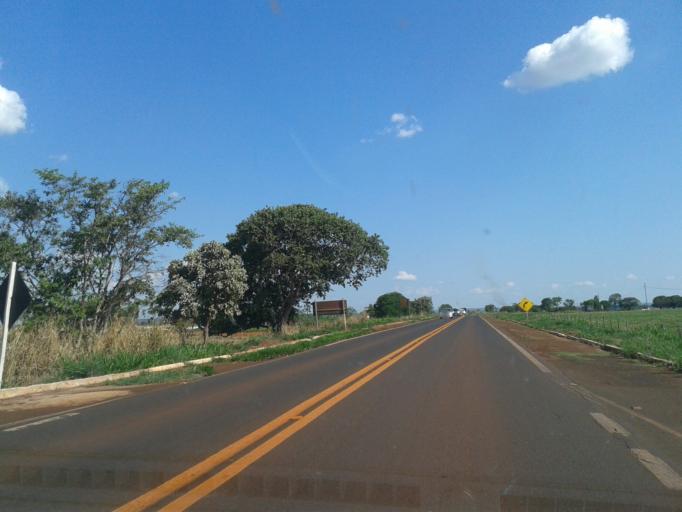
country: BR
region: Minas Gerais
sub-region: Ituiutaba
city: Ituiutaba
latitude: -18.9233
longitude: -49.4441
